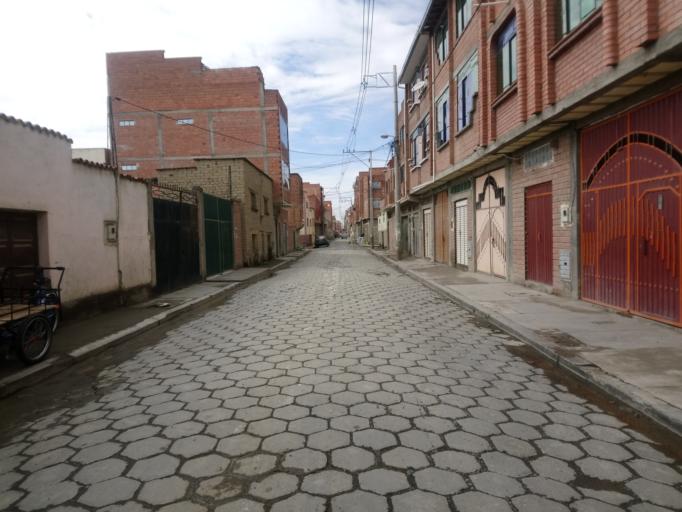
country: BO
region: La Paz
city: Achacachi
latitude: -16.0410
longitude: -68.6866
